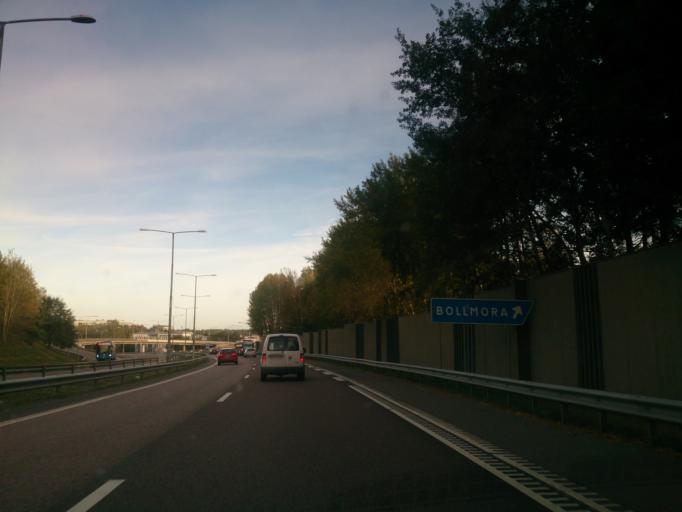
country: SE
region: Stockholm
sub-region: Tyreso Kommun
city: Bollmora
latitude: 59.2495
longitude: 18.2124
